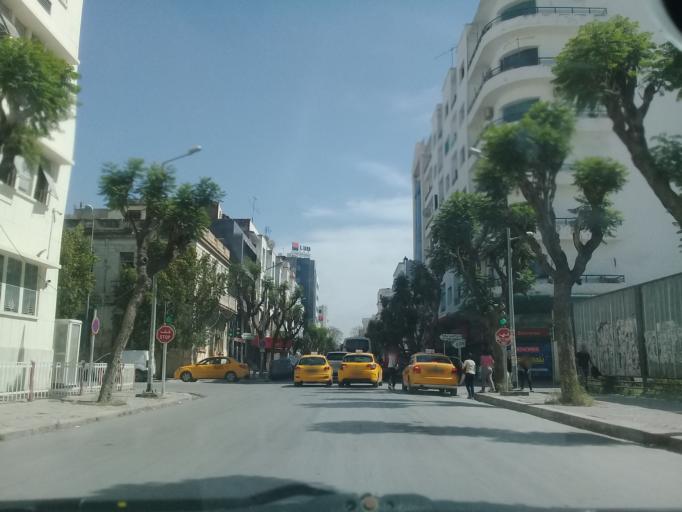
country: TN
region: Tunis
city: Tunis
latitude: 36.8136
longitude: 10.1792
